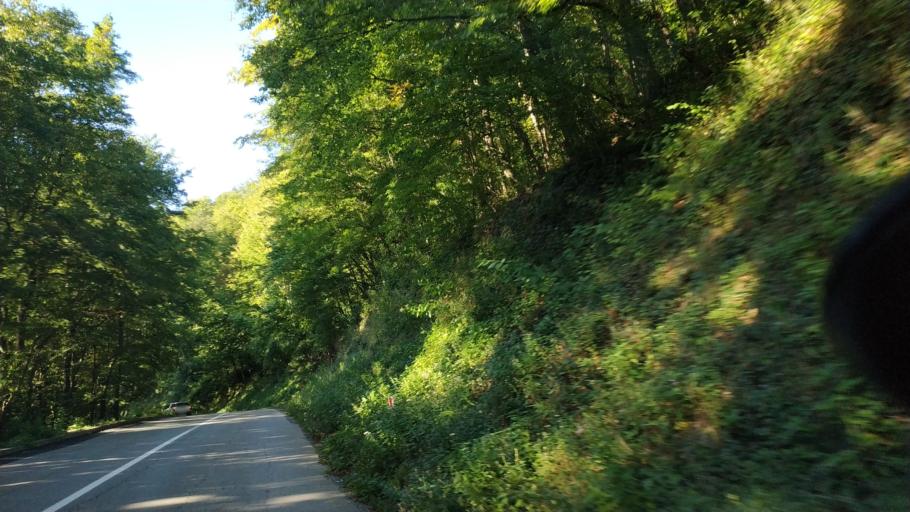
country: RS
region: Central Serbia
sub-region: Rasinski Okrug
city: Krusevac
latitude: 43.4488
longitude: 21.3608
